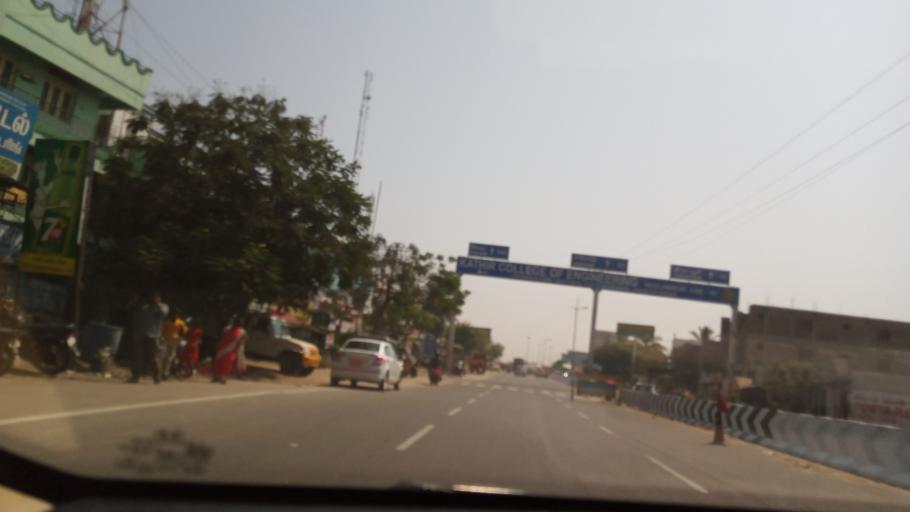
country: IN
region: Tamil Nadu
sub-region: Coimbatore
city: Irugur
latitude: 11.0610
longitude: 77.0858
